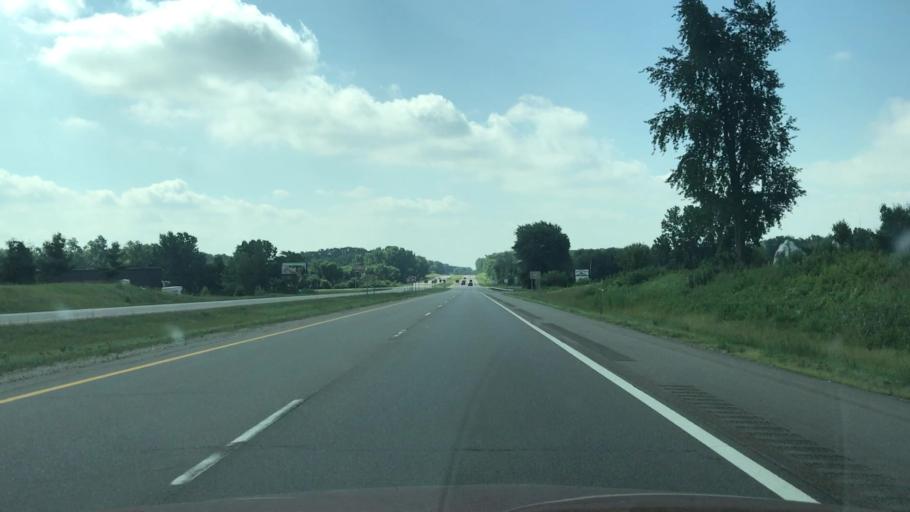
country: US
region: Michigan
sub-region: Kent County
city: Sparta
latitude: 43.1048
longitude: -85.6984
